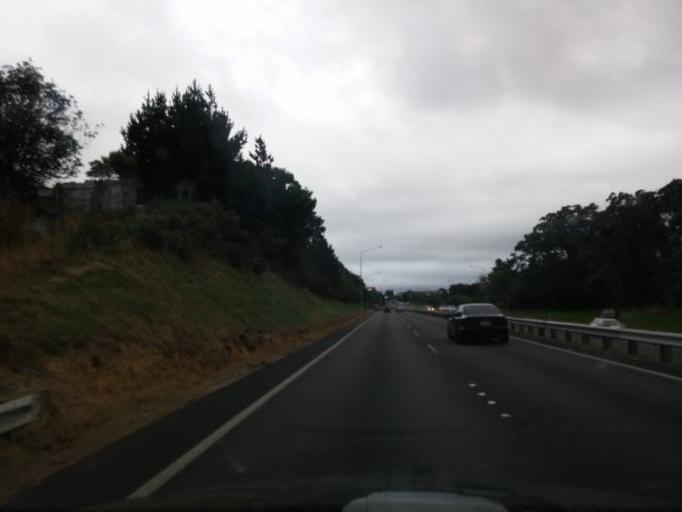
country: NZ
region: Wellington
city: Petone
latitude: -41.2170
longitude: 174.8118
